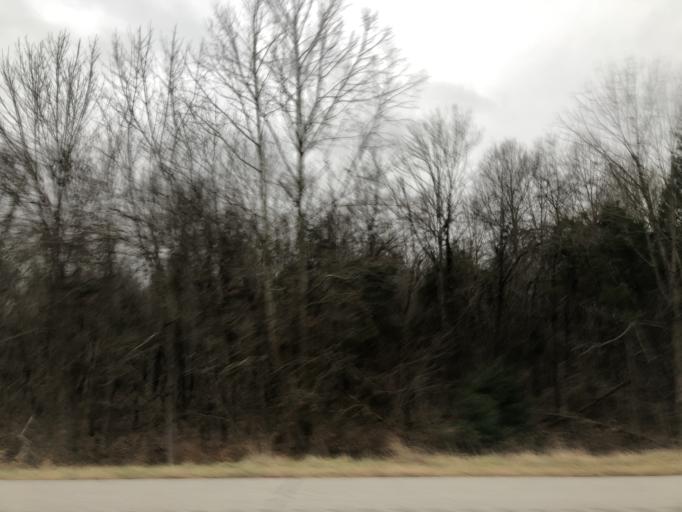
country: US
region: Illinois
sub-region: Johnson County
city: Vienna
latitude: 37.3652
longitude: -88.8024
